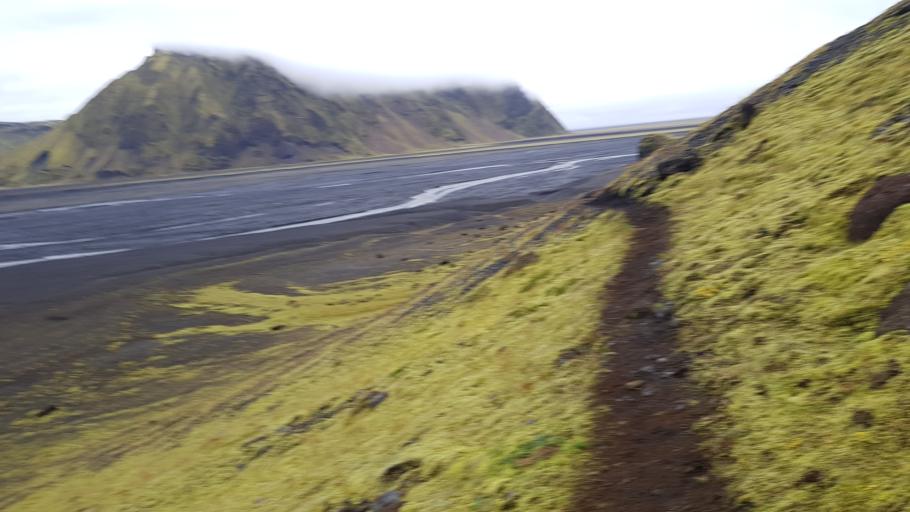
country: IS
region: South
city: Vestmannaeyjar
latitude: 63.5312
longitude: -18.8508
